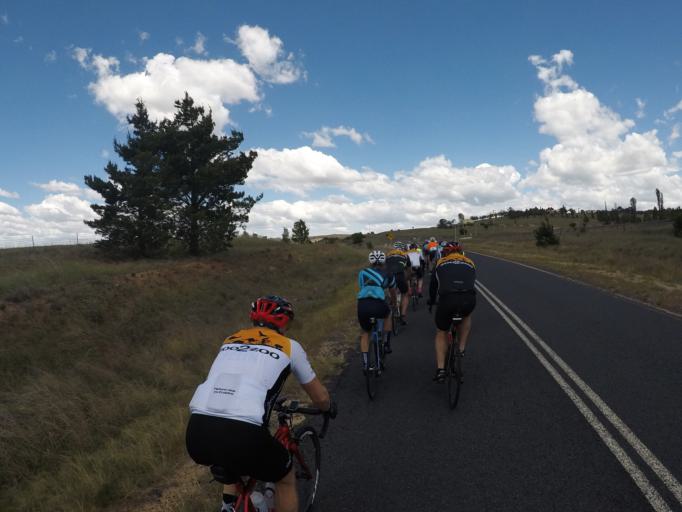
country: AU
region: New South Wales
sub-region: Blayney
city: Blayney
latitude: -33.5731
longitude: 149.4054
